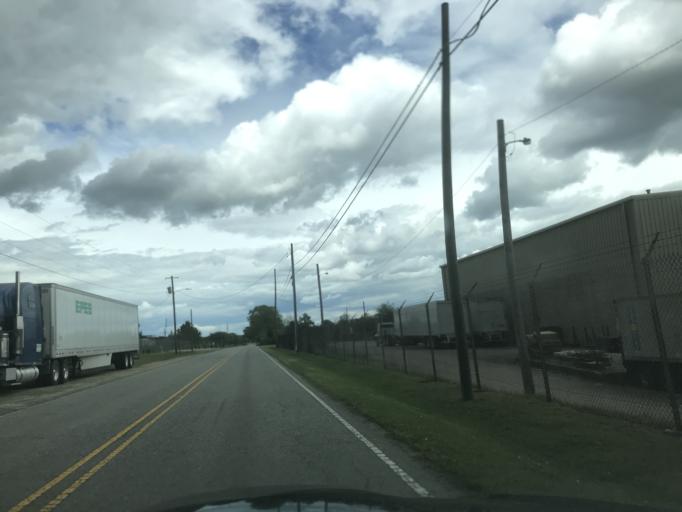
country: US
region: North Carolina
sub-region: Wake County
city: West Raleigh
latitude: 35.7920
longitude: -78.7104
